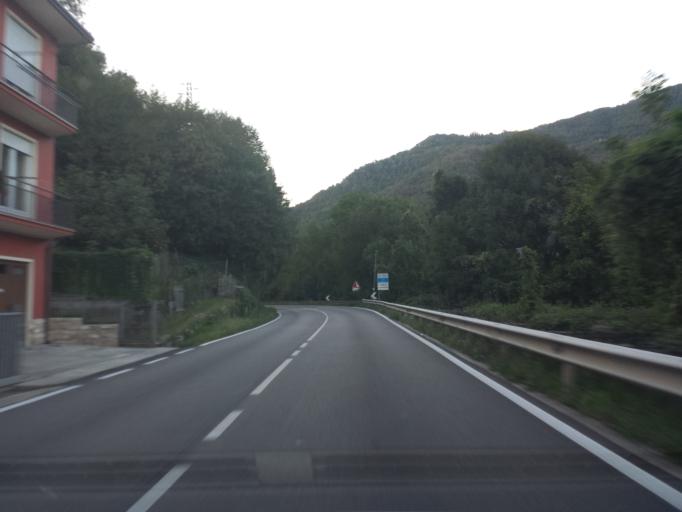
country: IT
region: Veneto
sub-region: Provincia di Vicenza
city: San Quirico
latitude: 45.6681
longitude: 11.2866
